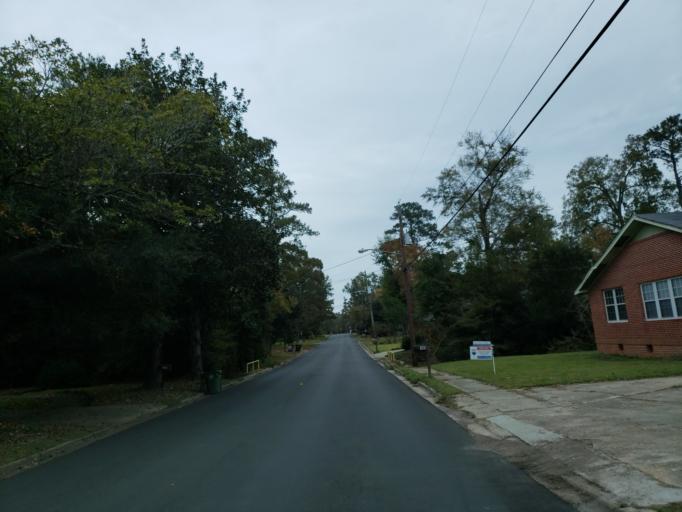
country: US
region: Mississippi
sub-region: Forrest County
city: Hattiesburg
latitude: 31.3255
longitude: -89.3178
